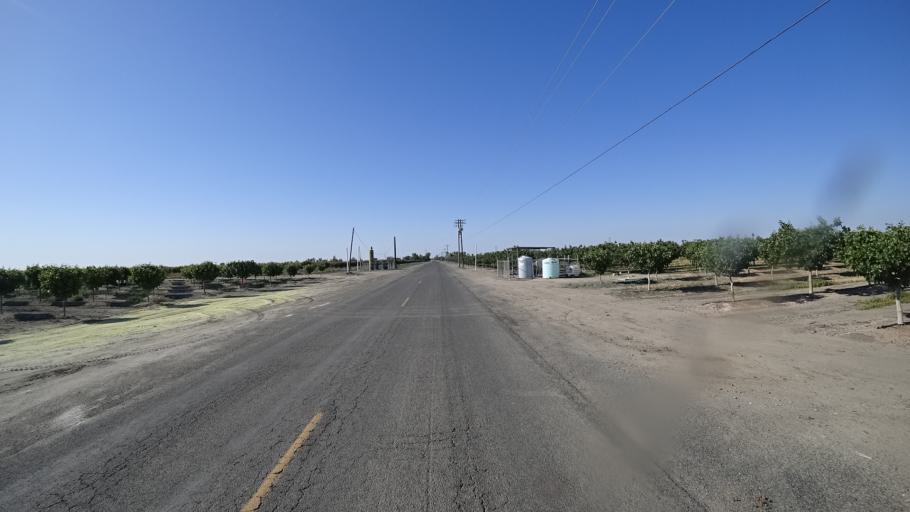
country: US
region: California
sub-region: Kings County
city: Corcoran
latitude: 36.1277
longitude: -119.5633
